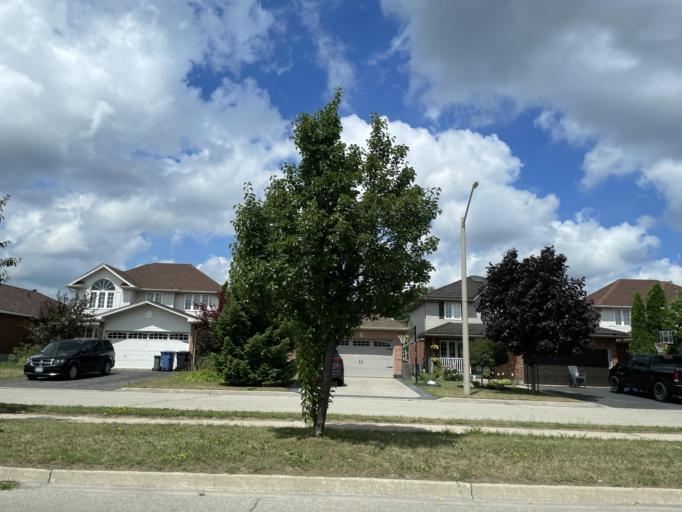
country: CA
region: Ontario
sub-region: Wellington County
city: Guelph
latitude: 43.4982
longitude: -80.1930
